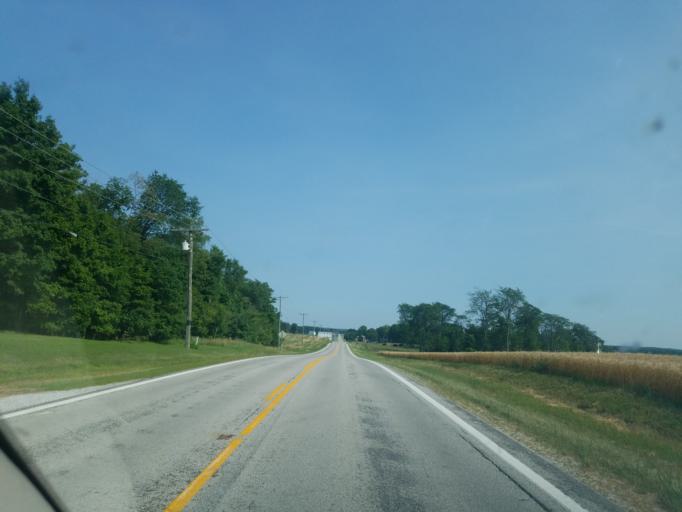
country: US
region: Ohio
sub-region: Wyandot County
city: Carey
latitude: 41.0132
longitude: -83.2843
